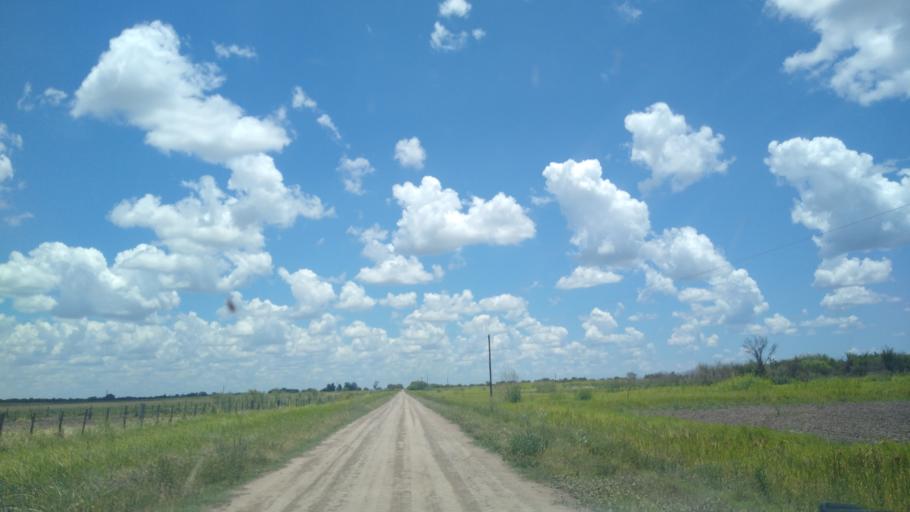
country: AR
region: Chaco
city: Presidencia Roque Saenz Pena
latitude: -26.7346
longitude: -60.3754
